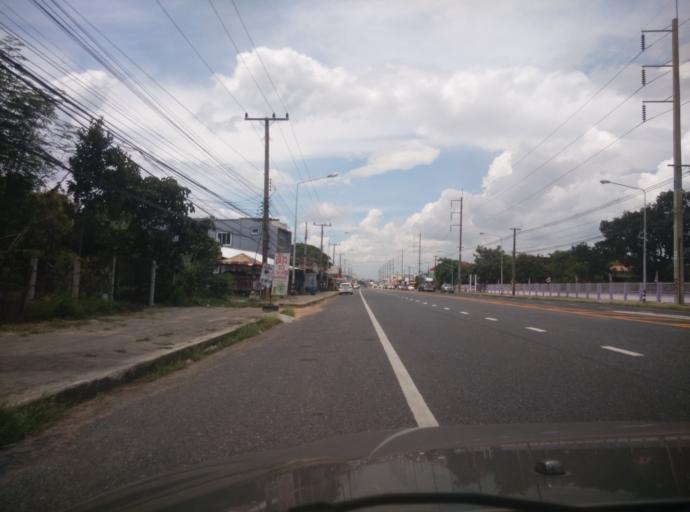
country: TH
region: Sisaket
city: Huai Thap Than
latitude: 15.0505
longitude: 104.0255
